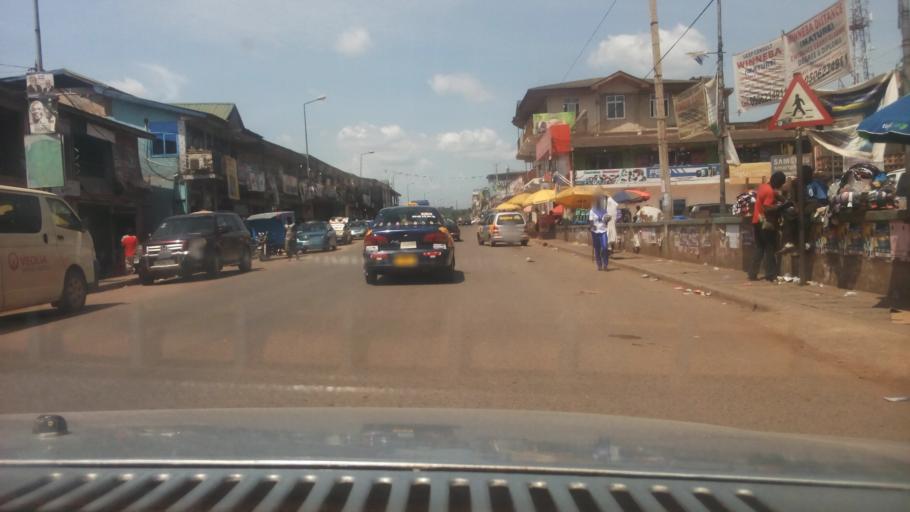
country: GH
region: Western
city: Tarkwa
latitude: 5.3055
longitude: -1.9953
